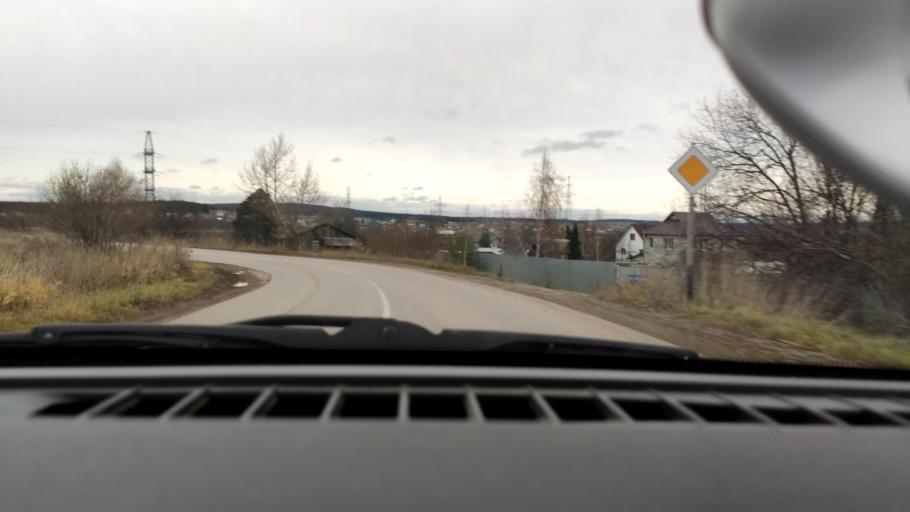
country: RU
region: Perm
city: Ferma
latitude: 57.9266
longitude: 56.3324
